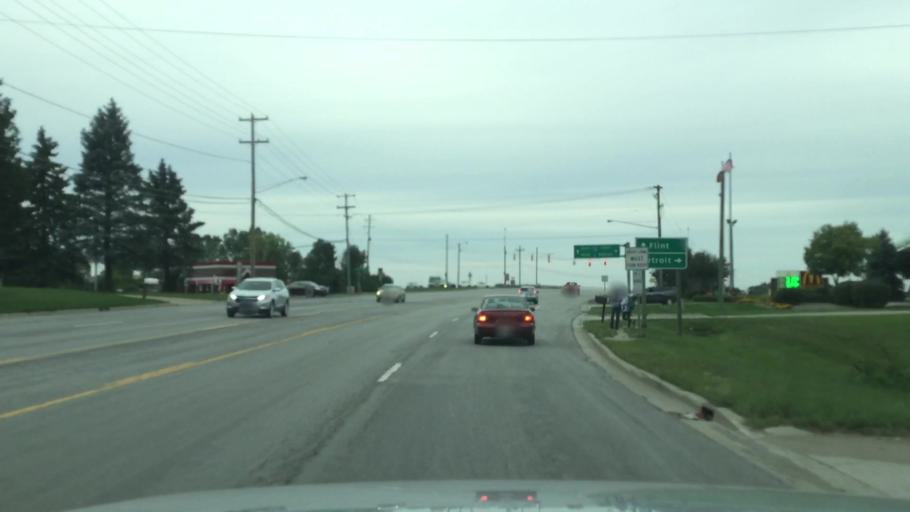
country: US
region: Michigan
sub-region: Genesee County
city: Grand Blanc
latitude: 42.8931
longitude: -83.6320
